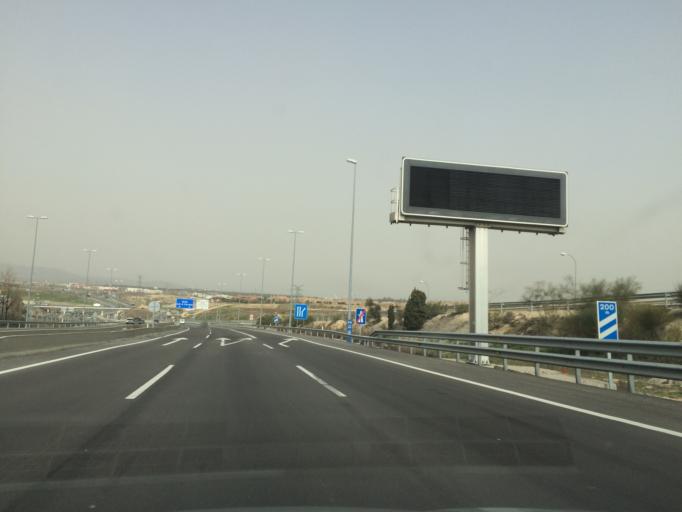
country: ES
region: Madrid
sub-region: Provincia de Madrid
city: Majadahonda
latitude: 40.4803
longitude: -3.8959
